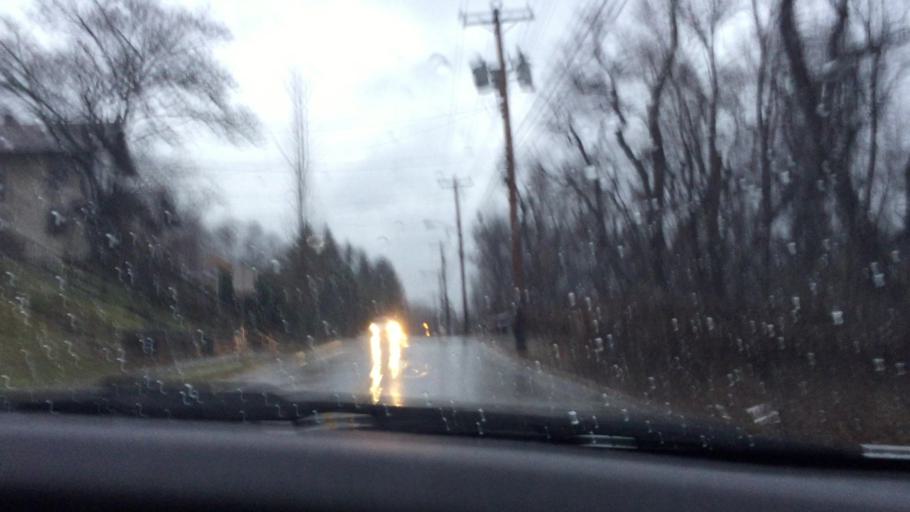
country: US
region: Pennsylvania
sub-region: Allegheny County
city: Ingram
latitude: 40.4515
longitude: -80.0575
